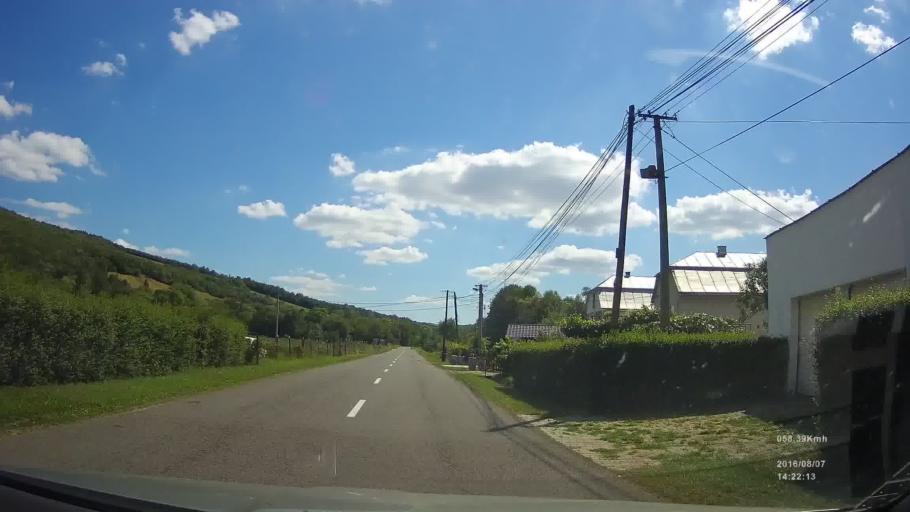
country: SK
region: Presovsky
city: Stropkov
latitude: 49.2759
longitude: 21.7517
